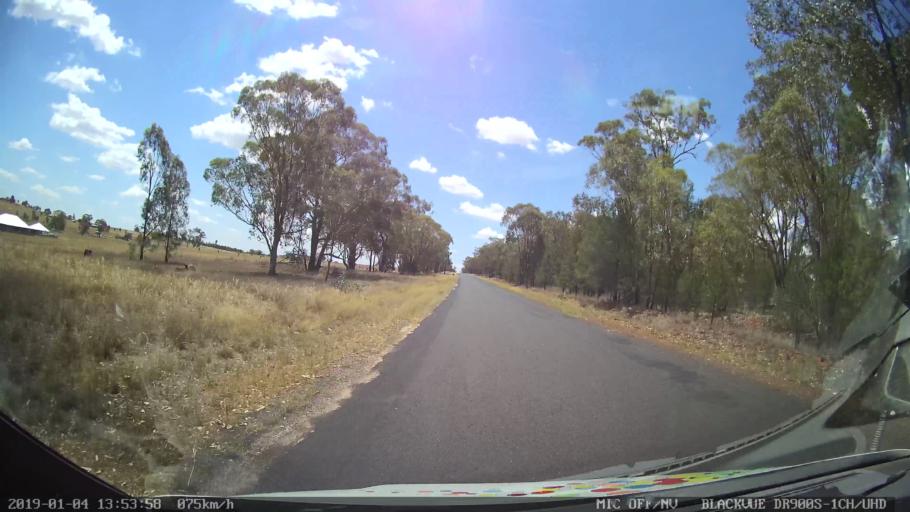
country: AU
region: New South Wales
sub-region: Dubbo Municipality
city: Dubbo
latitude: -32.3779
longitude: 148.5781
